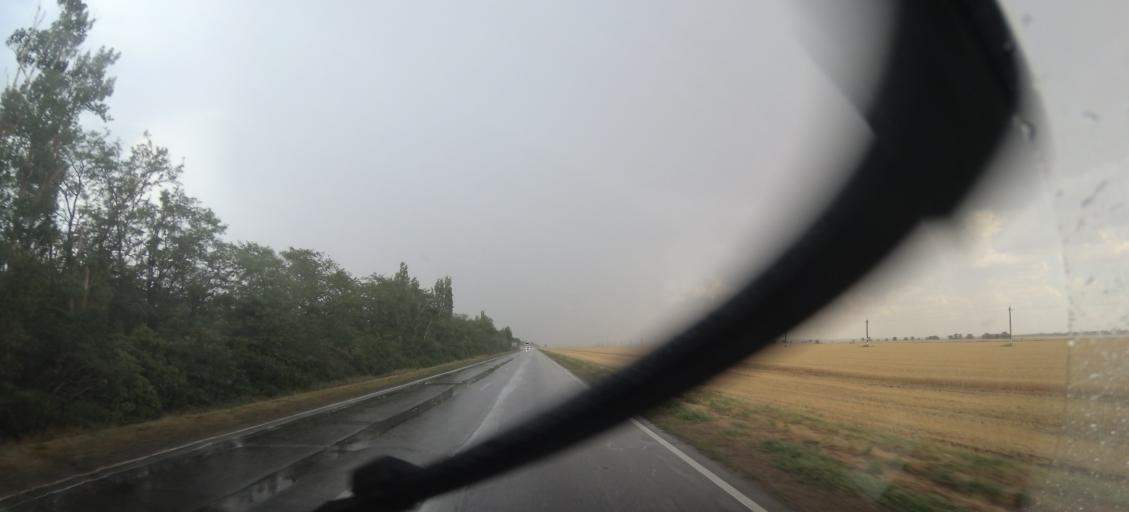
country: RU
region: Rostov
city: Proletarsk
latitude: 46.6633
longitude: 41.6873
